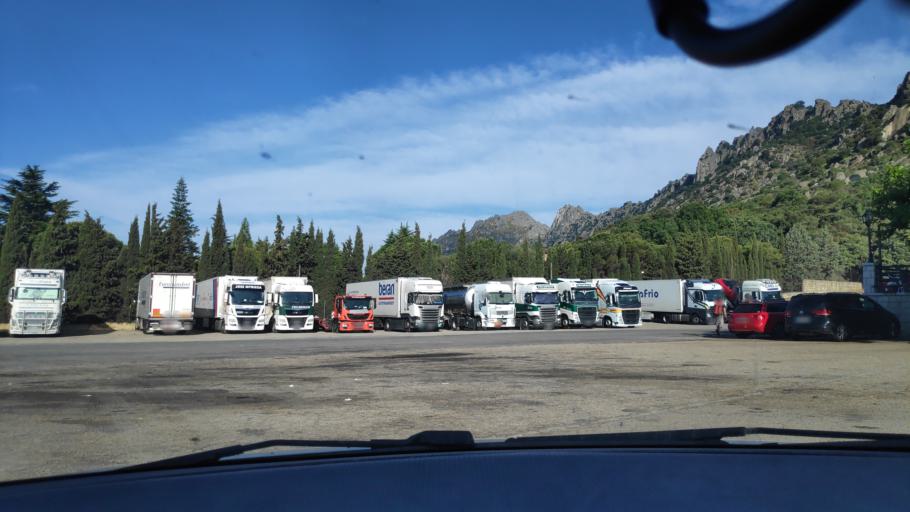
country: ES
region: Madrid
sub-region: Provincia de Madrid
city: La Cabrera
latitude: 40.8753
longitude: -3.6034
